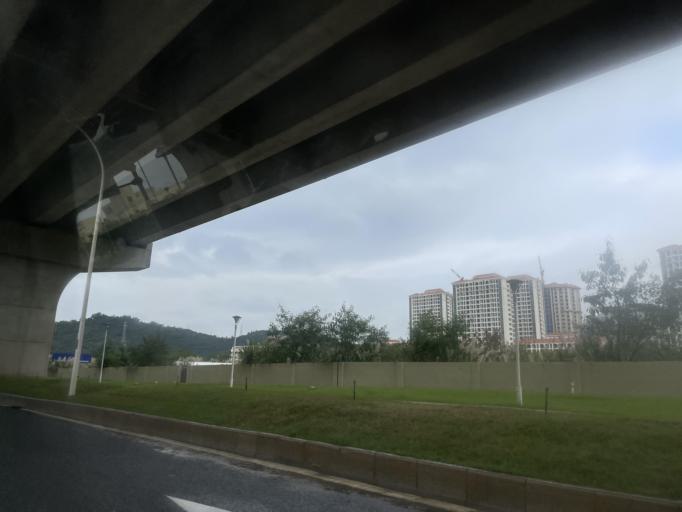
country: CN
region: Guangdong
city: Wanzai
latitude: 22.1765
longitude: 113.4893
